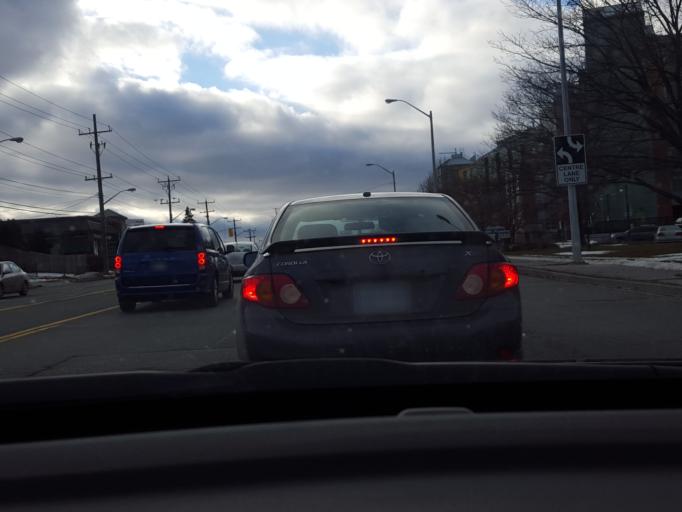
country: CA
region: Ontario
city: Scarborough
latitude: 43.7547
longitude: -79.2498
